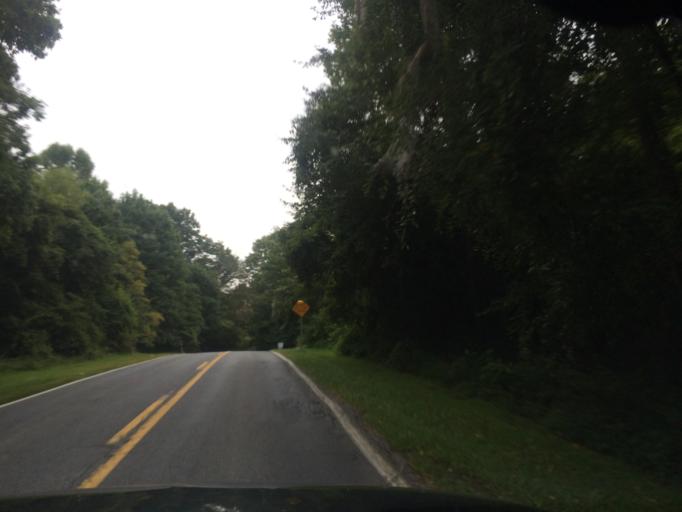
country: US
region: Maryland
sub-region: Montgomery County
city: Ashton-Sandy Spring
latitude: 39.1917
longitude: -77.0191
